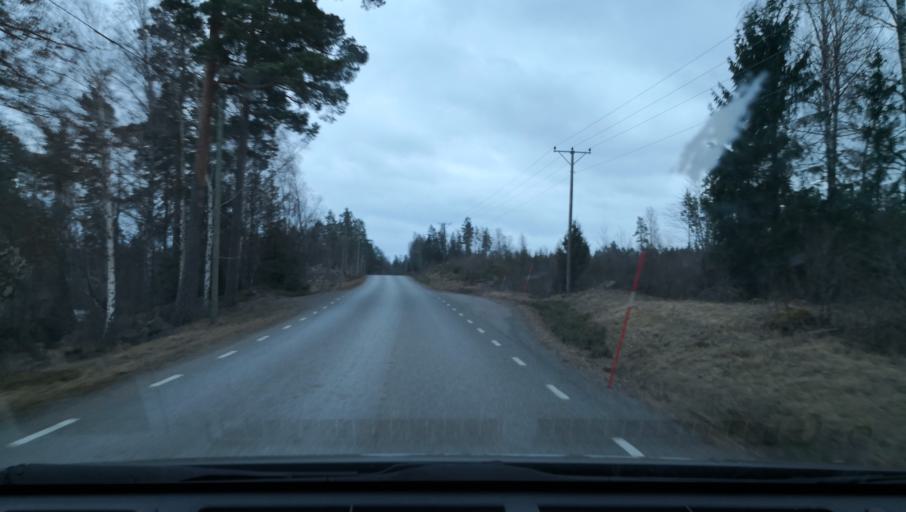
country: SE
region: OErebro
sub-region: Lindesbergs Kommun
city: Fellingsbro
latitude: 59.5739
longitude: 15.5683
